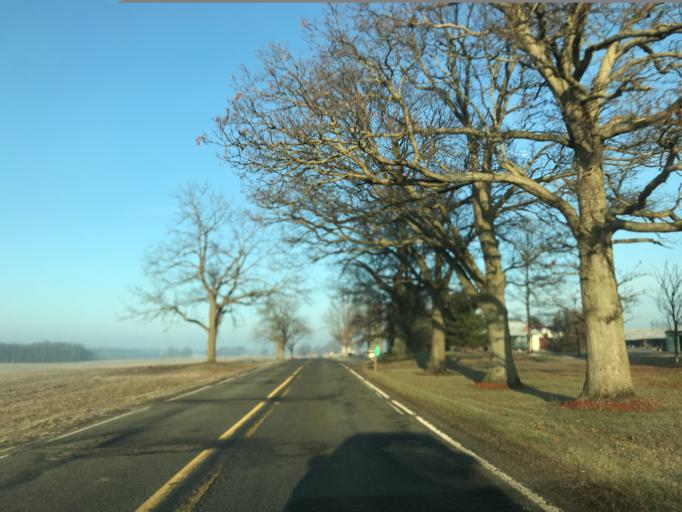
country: US
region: Michigan
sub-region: Ingham County
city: Leslie
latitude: 42.4130
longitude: -84.5012
